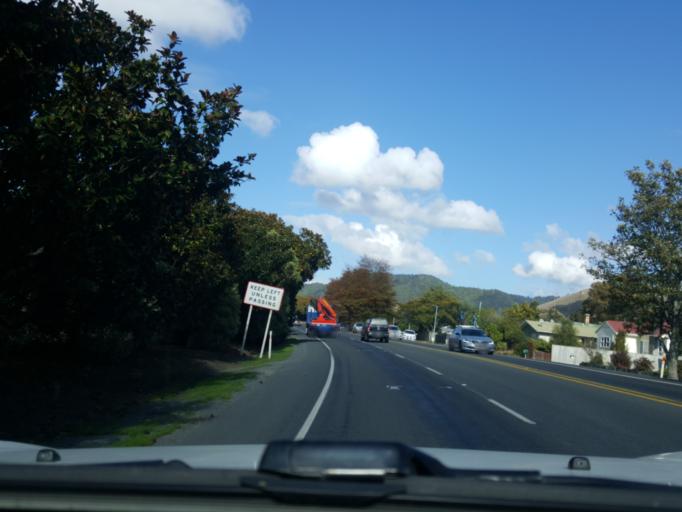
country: NZ
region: Waikato
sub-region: Waikato District
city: Ngaruawahia
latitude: -37.5810
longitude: 175.1591
